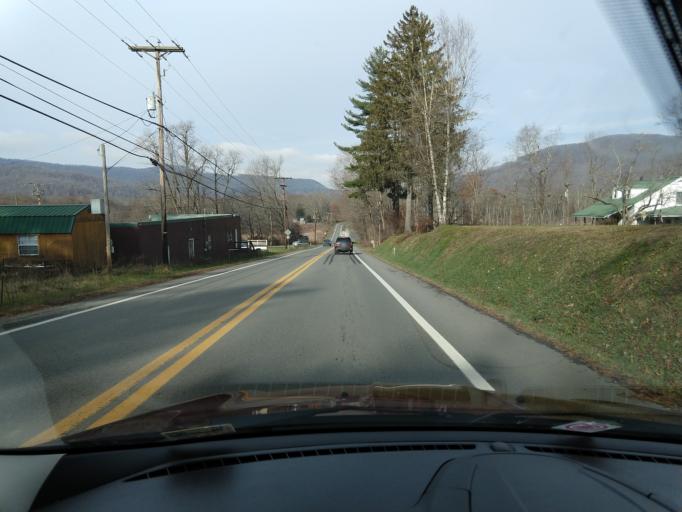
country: US
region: West Virginia
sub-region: Greenbrier County
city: Rainelle
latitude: 37.9545
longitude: -80.6784
